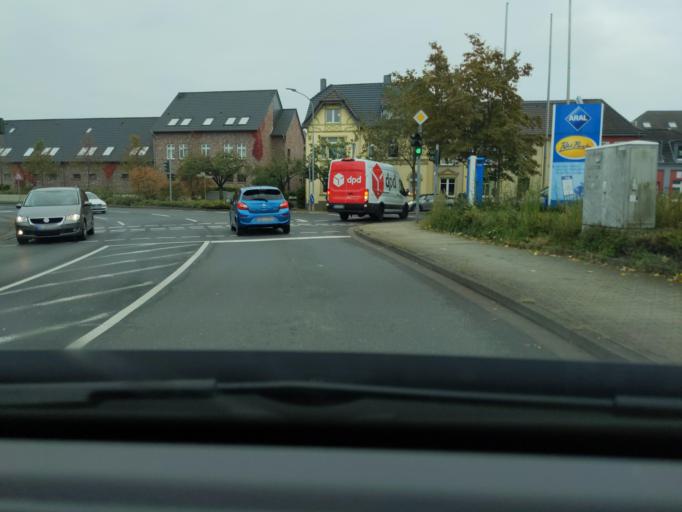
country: DE
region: North Rhine-Westphalia
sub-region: Regierungsbezirk Dusseldorf
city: Kaarst
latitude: 51.2185
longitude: 6.6060
